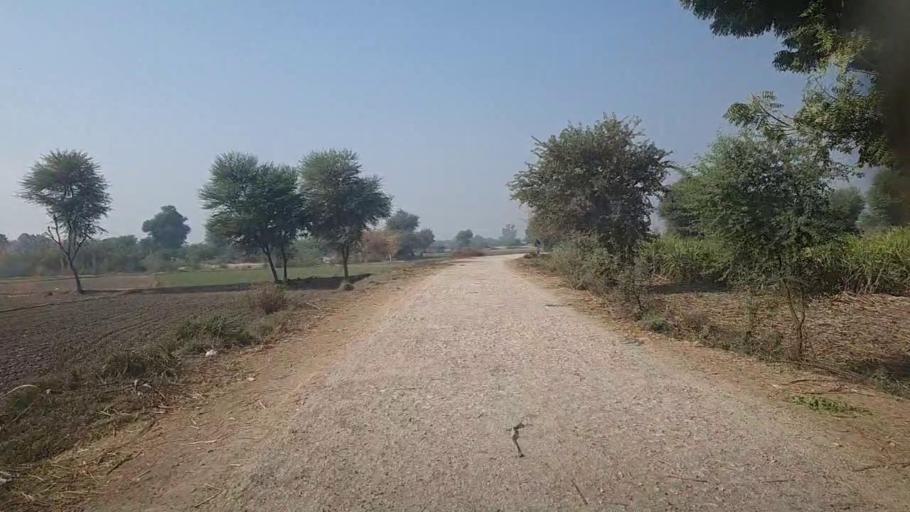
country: PK
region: Sindh
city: Karaundi
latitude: 26.9724
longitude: 68.4537
